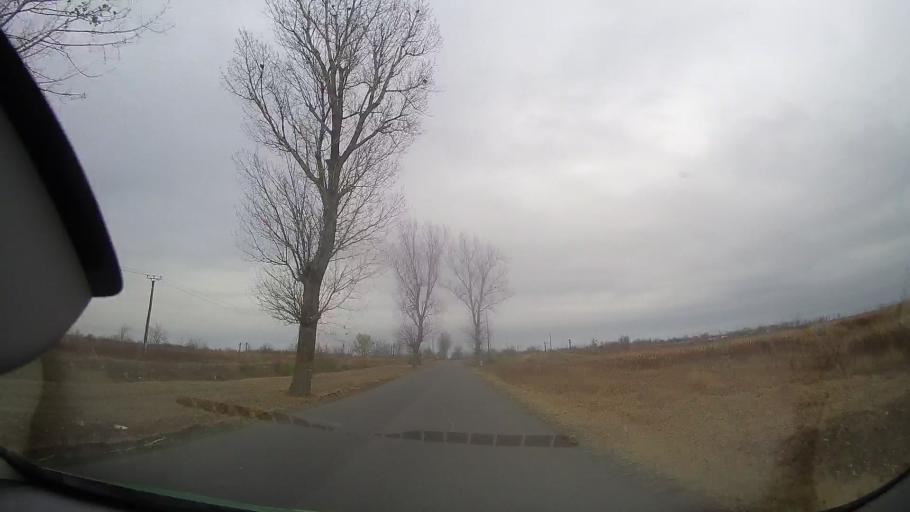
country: RO
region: Braila
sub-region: Comuna Rosiori
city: Rosiori
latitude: 44.8114
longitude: 27.3718
